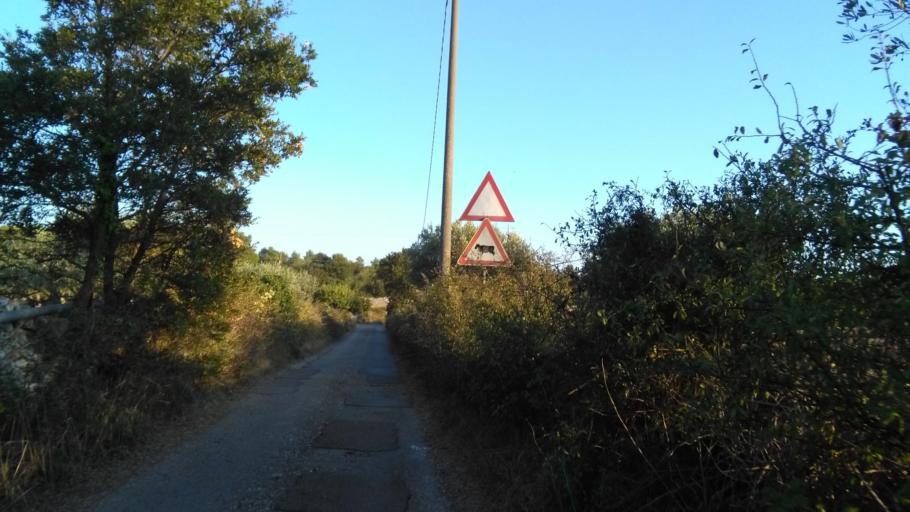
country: IT
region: Apulia
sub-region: Provincia di Bari
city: Putignano
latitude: 40.8271
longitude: 17.0776
